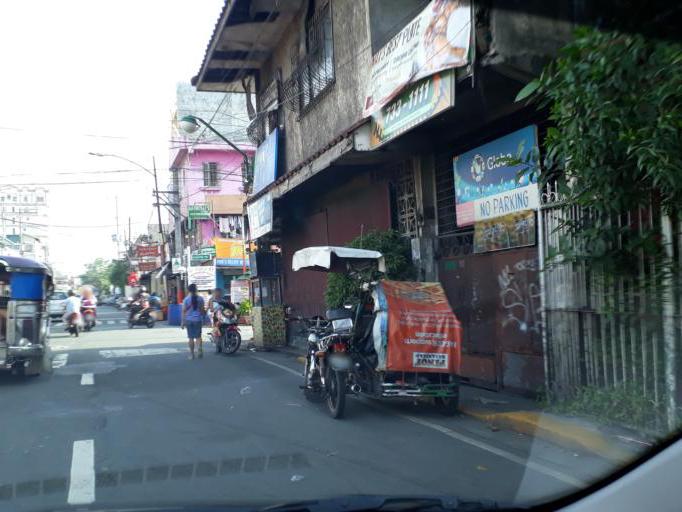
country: PH
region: Metro Manila
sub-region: City of Manila
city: Manila
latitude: 14.6255
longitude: 120.9732
